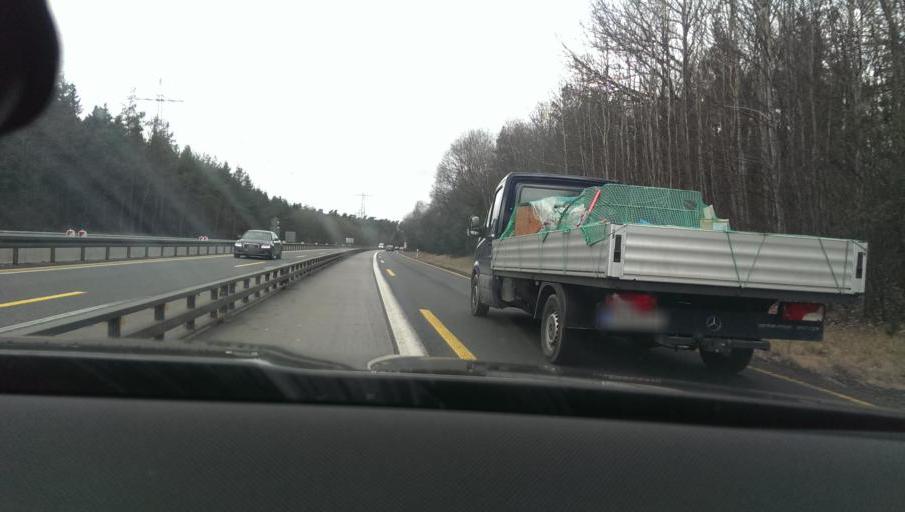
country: DE
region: Hesse
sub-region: Regierungsbezirk Kassel
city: Petersberg
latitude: 50.5939
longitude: 9.6868
